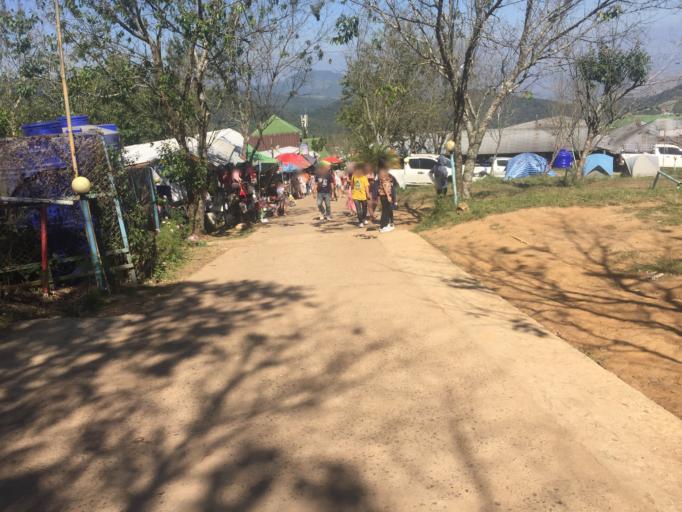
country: TH
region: Phetchabun
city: Lom Kao
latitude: 16.8969
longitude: 101.1056
